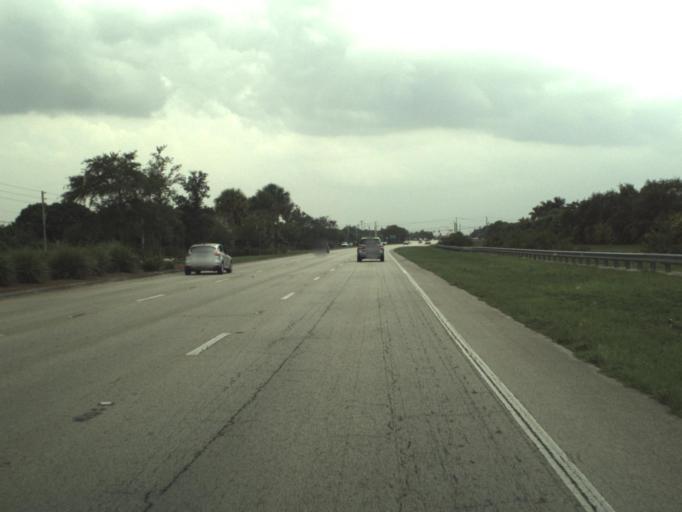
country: US
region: Florida
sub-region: Broward County
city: Southwest Ranches
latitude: 26.0701
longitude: -80.3140
